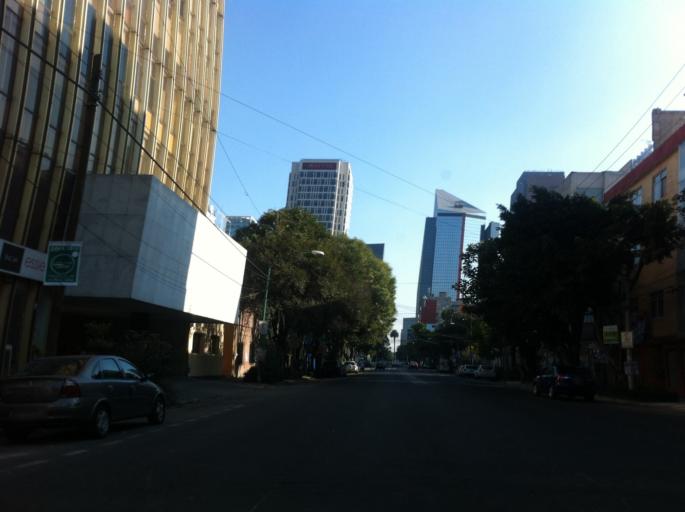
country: MX
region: Mexico City
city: Cuauhtemoc
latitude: 19.4330
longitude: -99.1659
